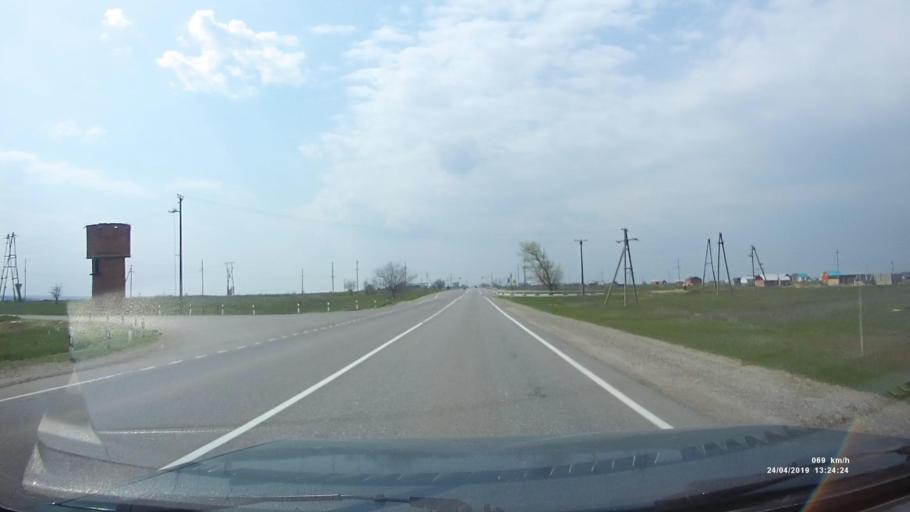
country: RU
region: Kalmykiya
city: Elista
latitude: 46.2841
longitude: 44.2553
